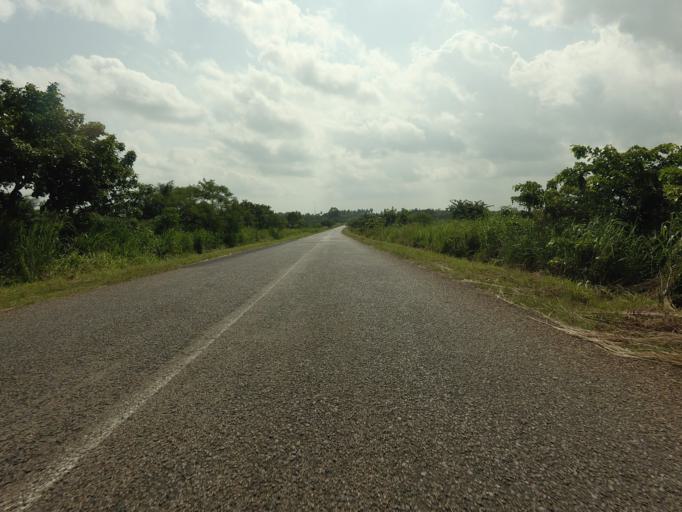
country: GH
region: Volta
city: Ho
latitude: 6.4098
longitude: 0.7645
